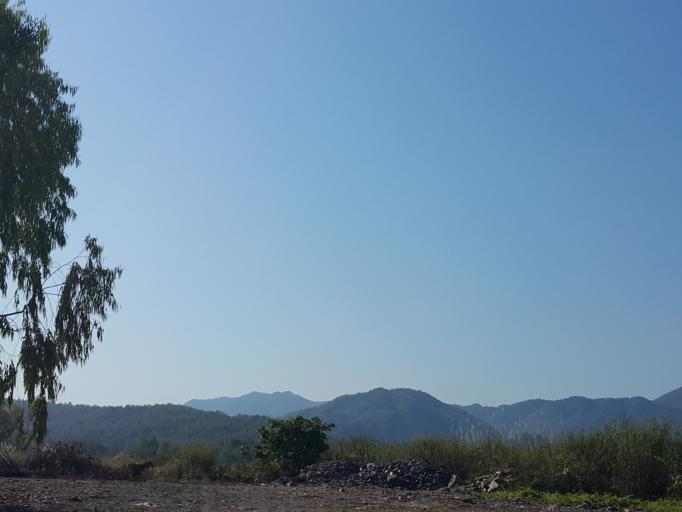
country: TH
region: Sukhothai
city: Thung Saliam
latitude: 17.3046
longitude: 99.4241
